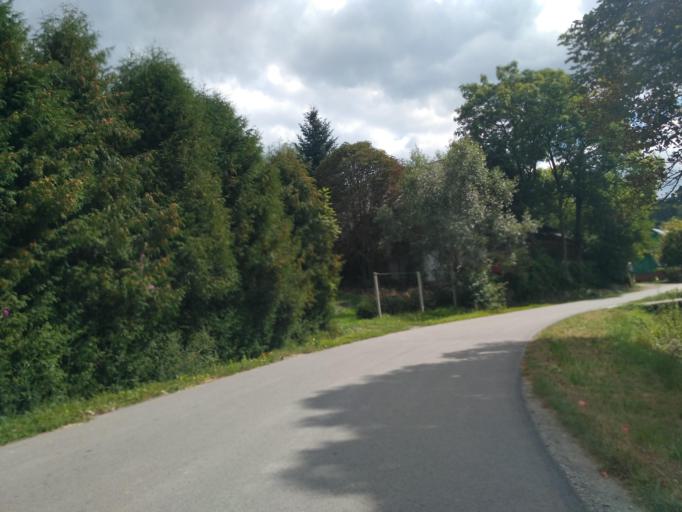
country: PL
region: Subcarpathian Voivodeship
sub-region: Powiat rzeszowski
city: Dynow
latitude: 49.7753
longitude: 22.2420
